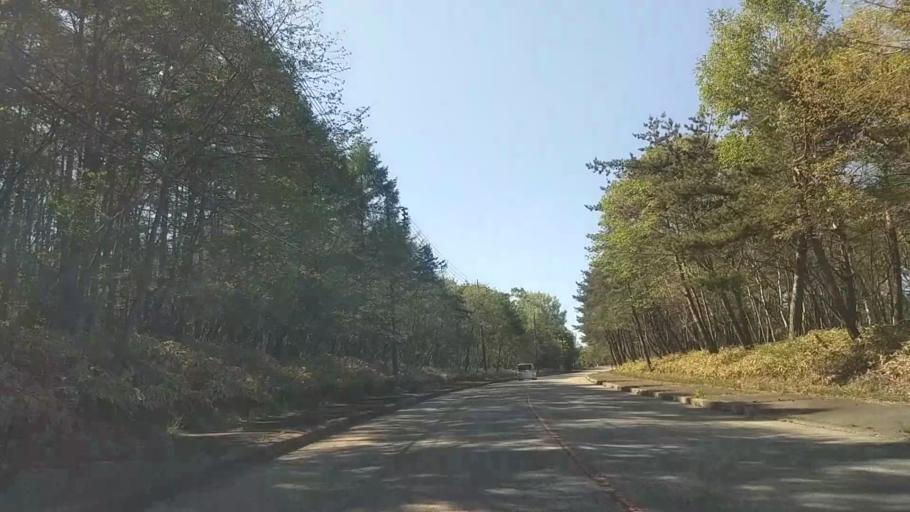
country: JP
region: Yamanashi
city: Nirasaki
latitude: 35.9321
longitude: 138.4446
